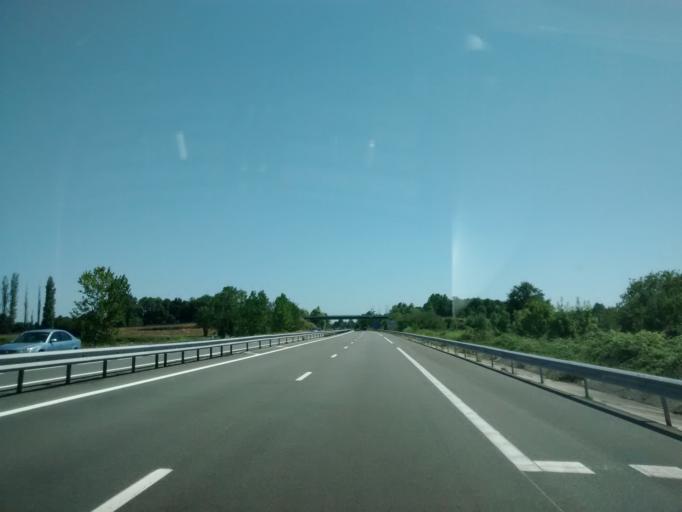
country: FR
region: Aquitaine
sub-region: Departement de la Gironde
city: Saint-Medard-de-Guizieres
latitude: 45.0084
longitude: -0.0899
